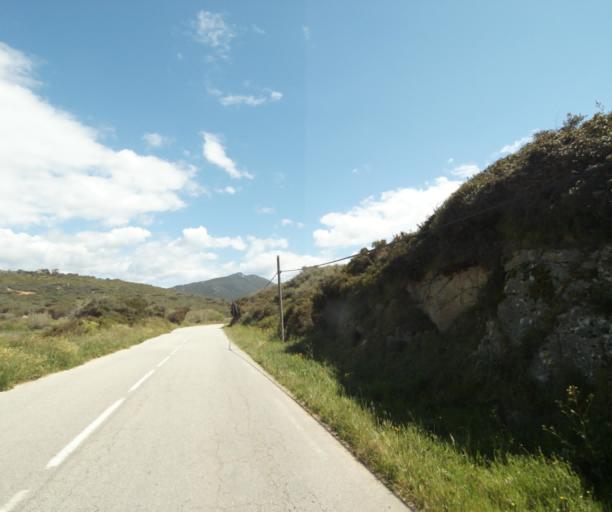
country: FR
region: Corsica
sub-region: Departement de la Corse-du-Sud
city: Propriano
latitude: 41.6584
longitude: 8.8980
